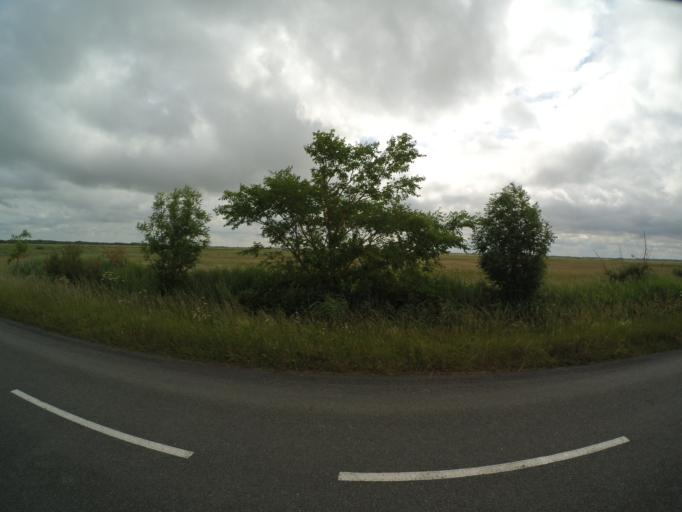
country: FR
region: Poitou-Charentes
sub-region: Departement de la Charente-Maritime
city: Yves
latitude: 46.0295
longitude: -1.0482
